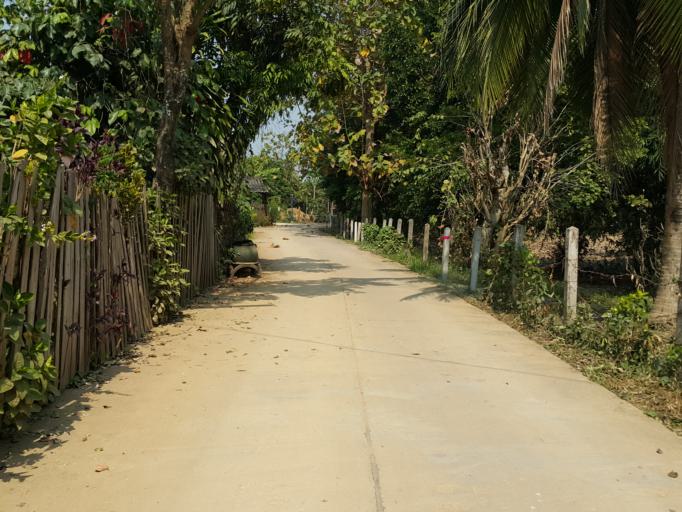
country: TH
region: Sukhothai
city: Thung Saliam
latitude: 17.3235
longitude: 99.5128
